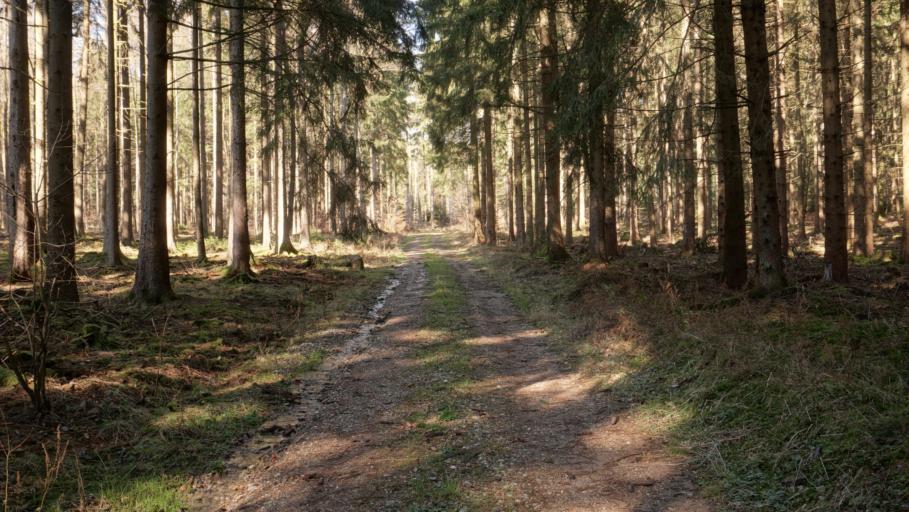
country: DE
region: Baden-Wuerttemberg
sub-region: Karlsruhe Region
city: Fahrenbach
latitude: 49.4503
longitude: 9.1169
